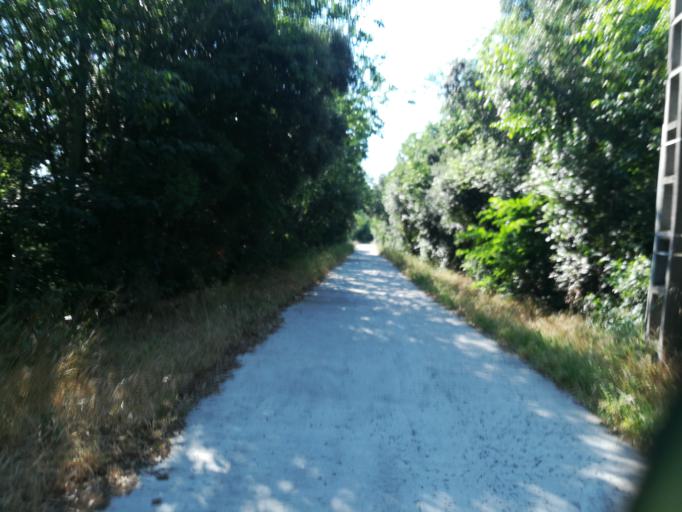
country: FR
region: Languedoc-Roussillon
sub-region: Departement des Pyrenees-Orientales
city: Reiners
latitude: 42.4970
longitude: 2.7152
